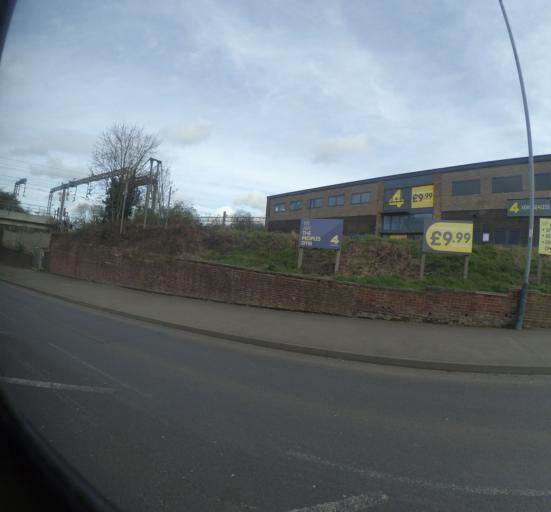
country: GB
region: England
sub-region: Warwickshire
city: Rugby
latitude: 52.3802
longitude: -1.2647
